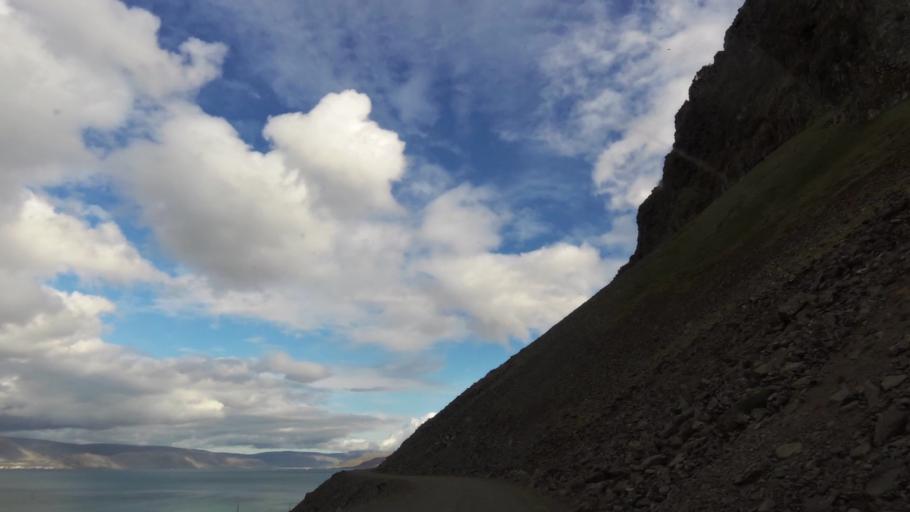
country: IS
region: West
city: Olafsvik
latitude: 65.5998
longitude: -24.1388
